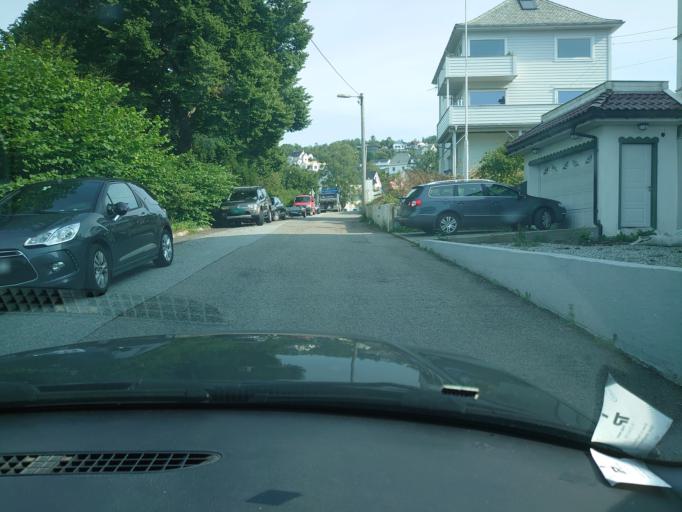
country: NO
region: Hordaland
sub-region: Bergen
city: Bergen
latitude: 60.3830
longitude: 5.3015
